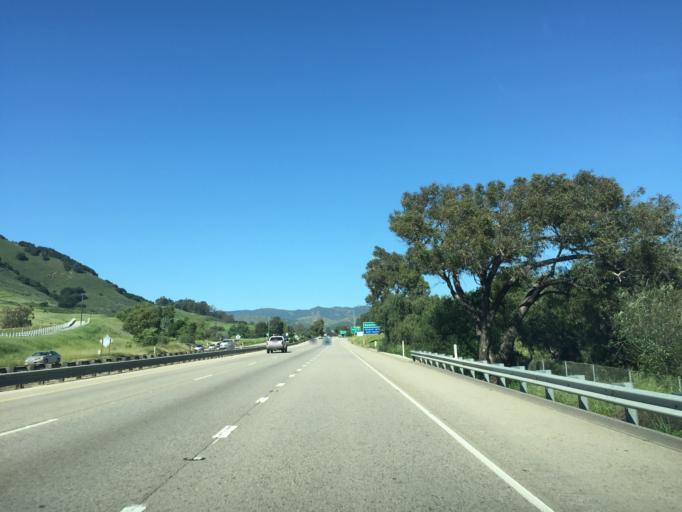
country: US
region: California
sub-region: San Luis Obispo County
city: San Luis Obispo
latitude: 35.2703
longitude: -120.6726
